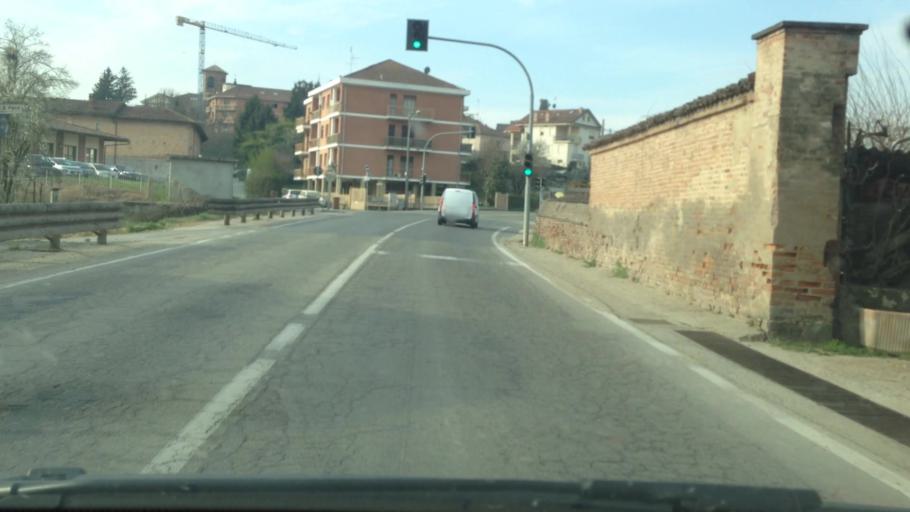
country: IT
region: Piedmont
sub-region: Provincia di Asti
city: San Damiano d'Asti
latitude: 44.8392
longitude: 8.0668
